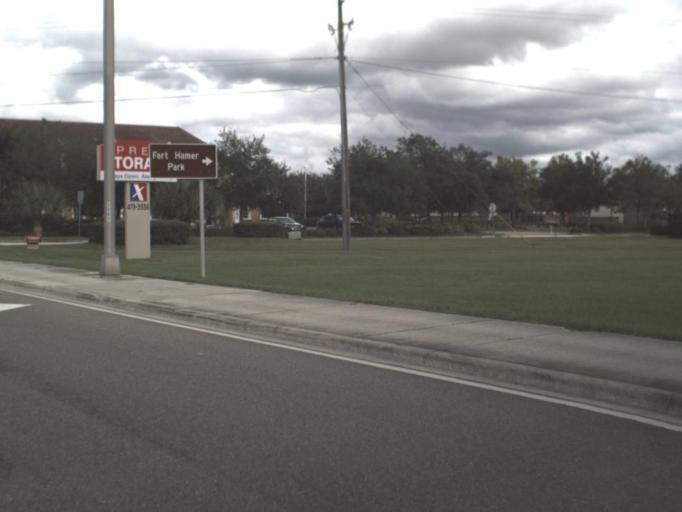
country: US
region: Florida
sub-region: Manatee County
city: Ellenton
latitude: 27.5417
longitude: -82.4791
